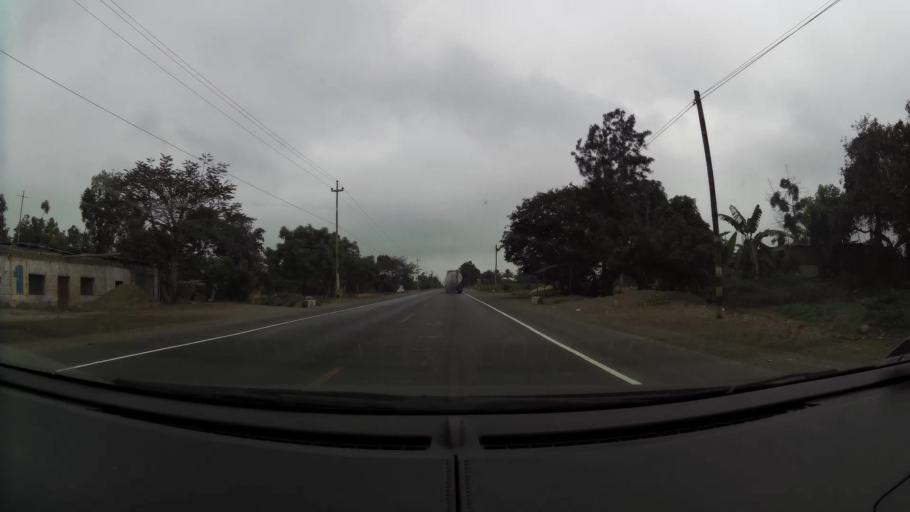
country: PE
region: La Libertad
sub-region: Viru
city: Viru
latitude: -8.4364
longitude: -78.7634
